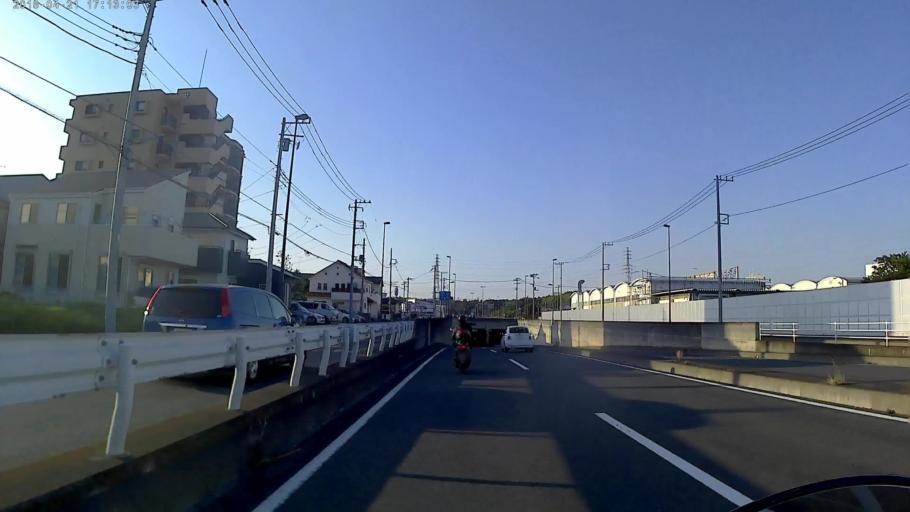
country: JP
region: Kanagawa
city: Fujisawa
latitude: 35.4051
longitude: 139.4409
